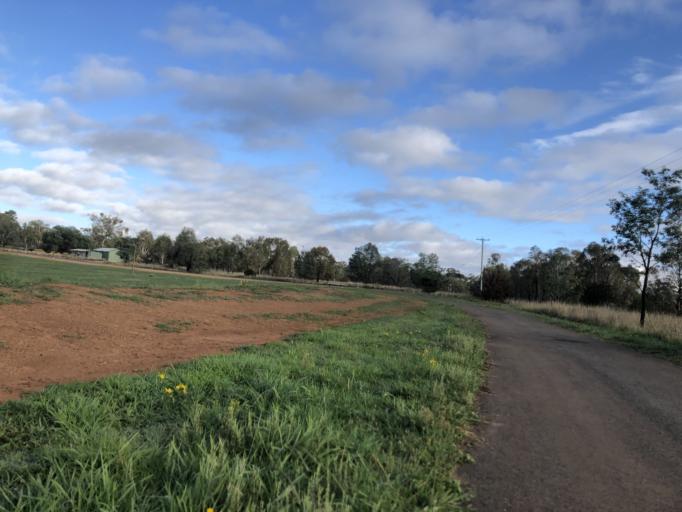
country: AU
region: New South Wales
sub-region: Orange Municipality
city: Orange
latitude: -33.3264
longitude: 149.0919
